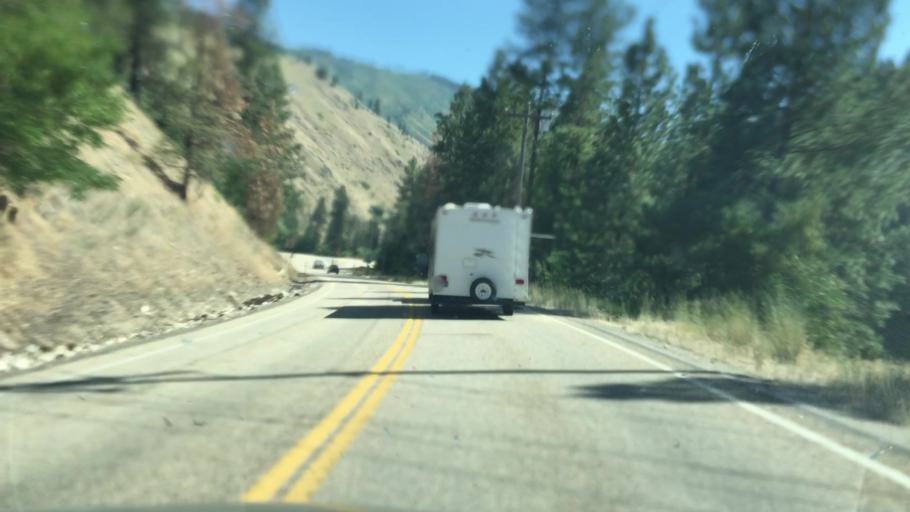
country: US
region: Idaho
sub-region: Boise County
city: Idaho City
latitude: 44.0506
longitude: -116.1328
